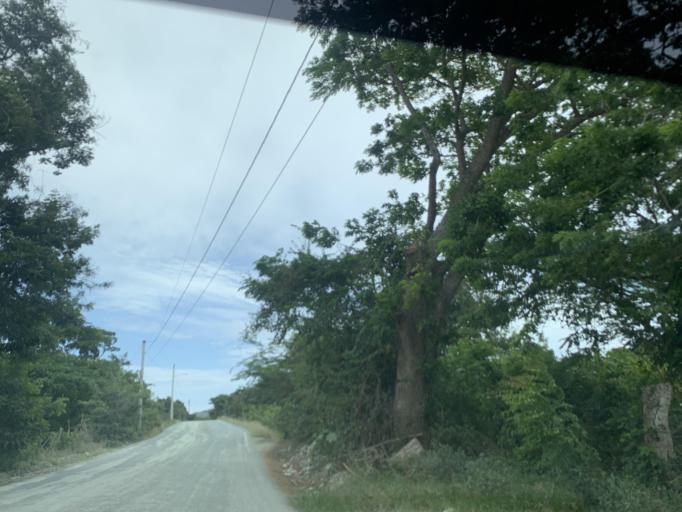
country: DO
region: Puerto Plata
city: Imbert
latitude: 19.8240
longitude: -70.7848
